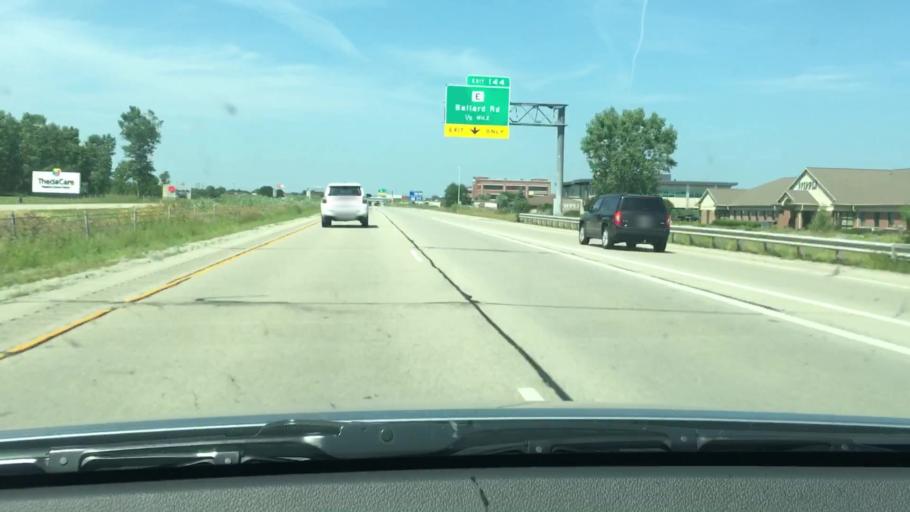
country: US
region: Wisconsin
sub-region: Outagamie County
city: Kimberly
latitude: 44.2982
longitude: -88.3629
